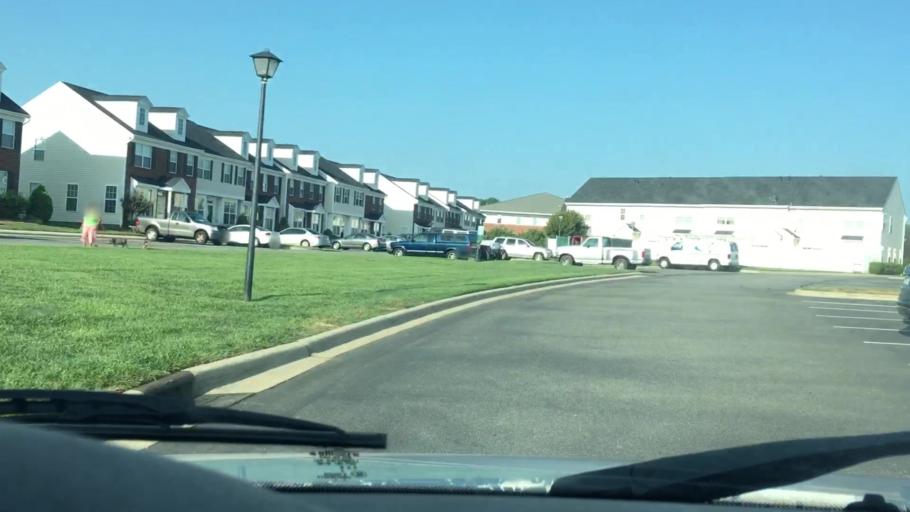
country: US
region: North Carolina
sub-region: Lincoln County
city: Lowesville
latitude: 35.4409
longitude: -80.9969
